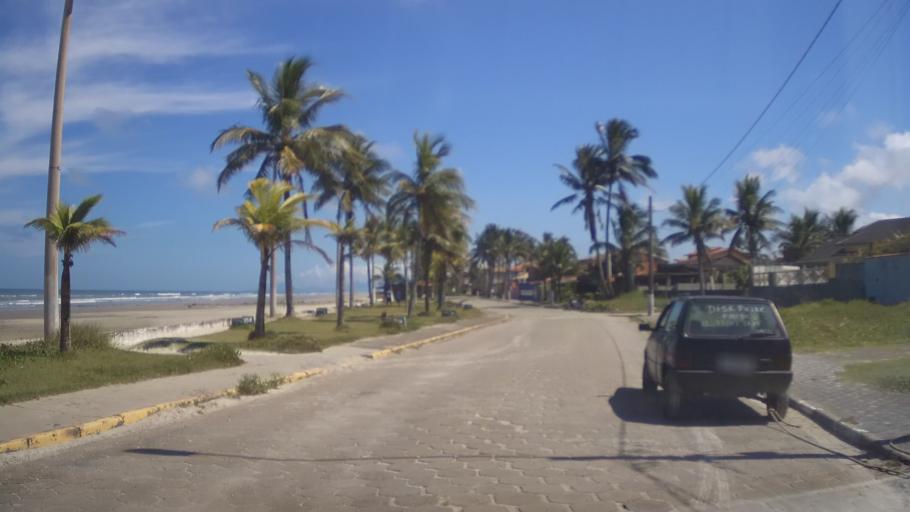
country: BR
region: Sao Paulo
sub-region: Itanhaem
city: Itanhaem
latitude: -24.1420
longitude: -46.7080
